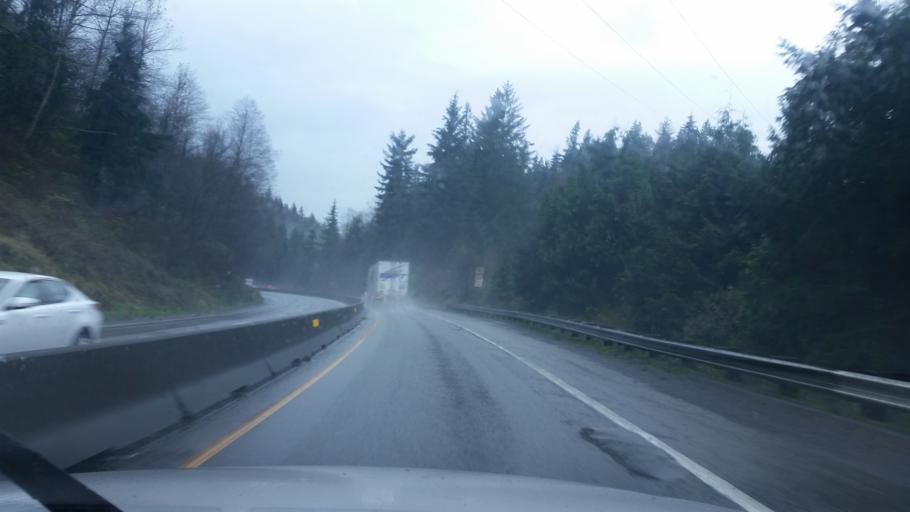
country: US
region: Washington
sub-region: King County
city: Hobart
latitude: 47.4574
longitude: -121.9501
